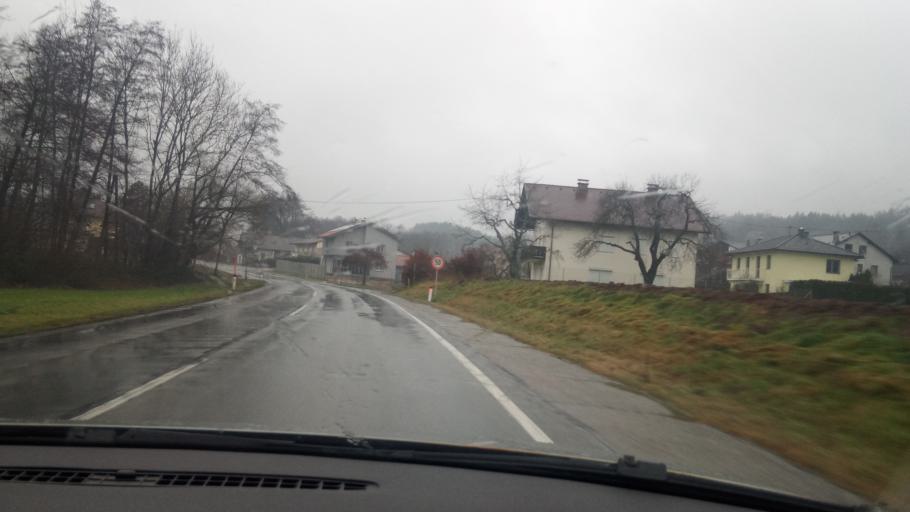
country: AT
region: Carinthia
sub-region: Politischer Bezirk Klagenfurt Land
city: Kottmannsdorf
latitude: 46.5888
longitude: 14.2231
